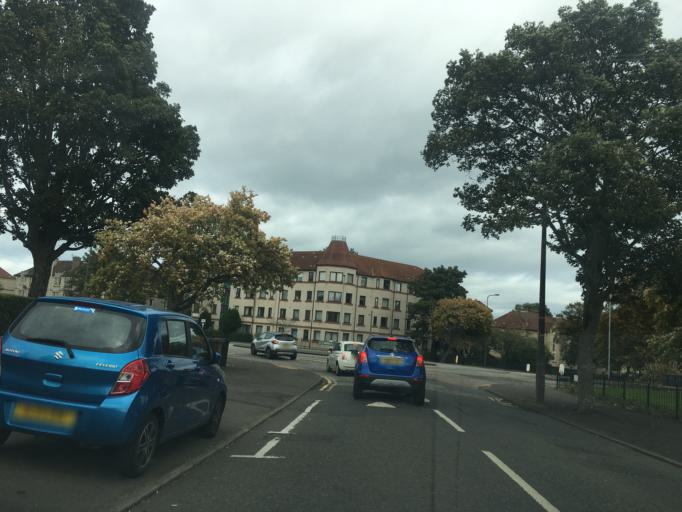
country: GB
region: Scotland
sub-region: West Lothian
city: Seafield
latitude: 55.9617
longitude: -3.1534
